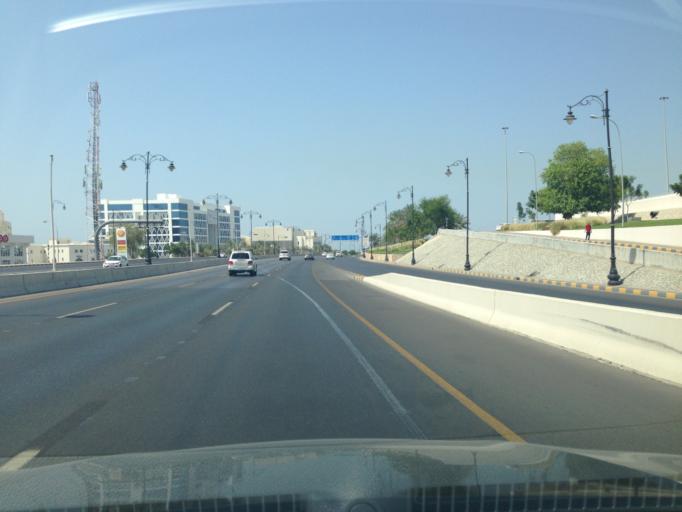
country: OM
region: Muhafazat Masqat
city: Bawshar
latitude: 23.5899
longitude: 58.4082
